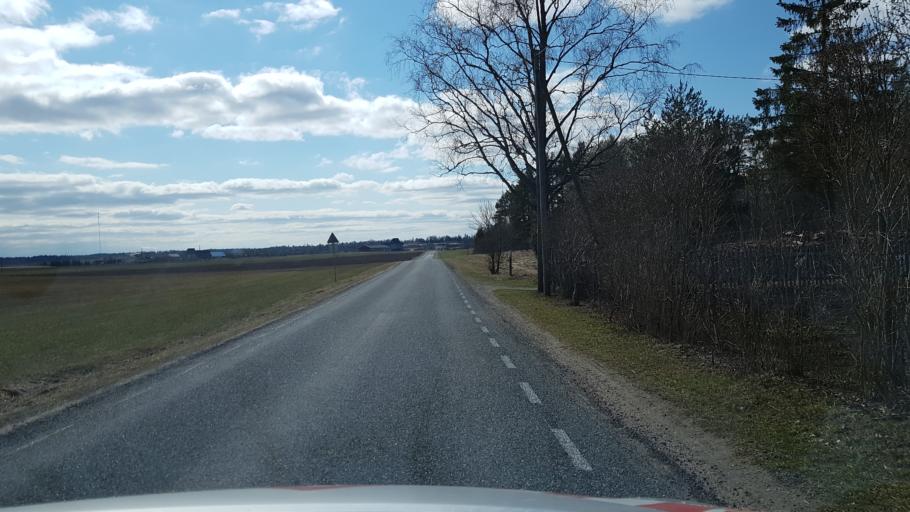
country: EE
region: Laeaene-Virumaa
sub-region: Tapa vald
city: Tapa
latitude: 59.2530
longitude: 25.7053
